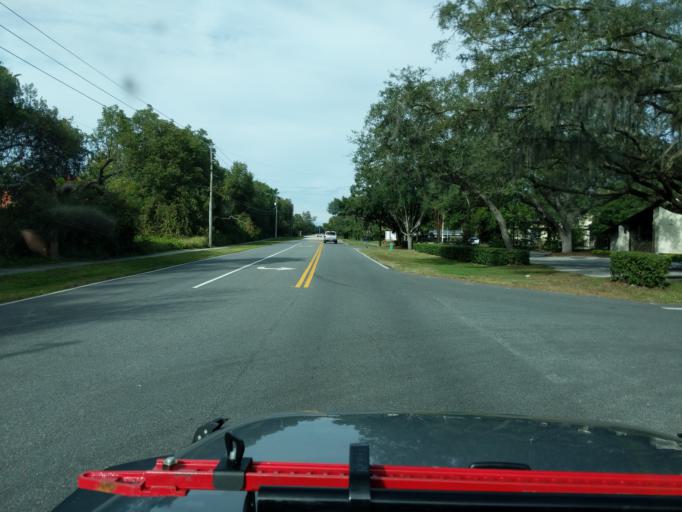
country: US
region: Florida
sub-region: Orange County
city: Lake Butler
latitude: 28.5181
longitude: -81.5415
